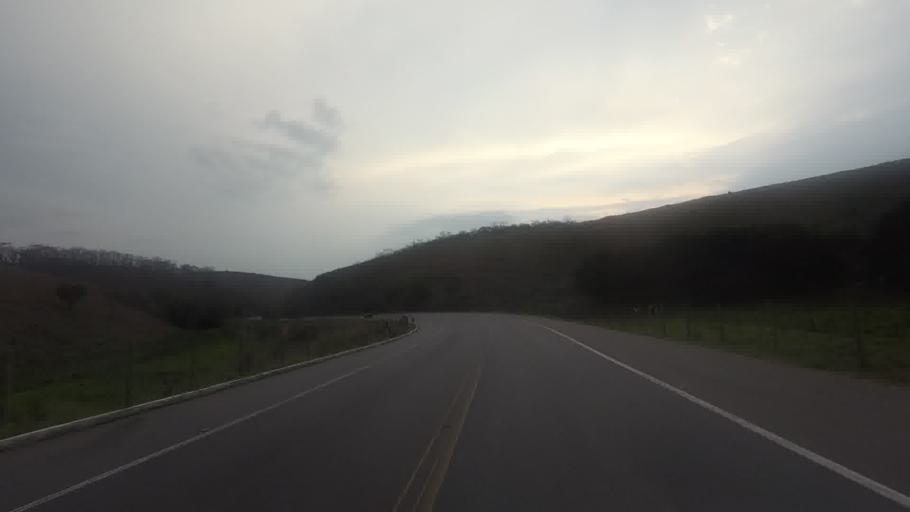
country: BR
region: Rio de Janeiro
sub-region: Carmo
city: Carmo
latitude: -21.8081
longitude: -42.5845
